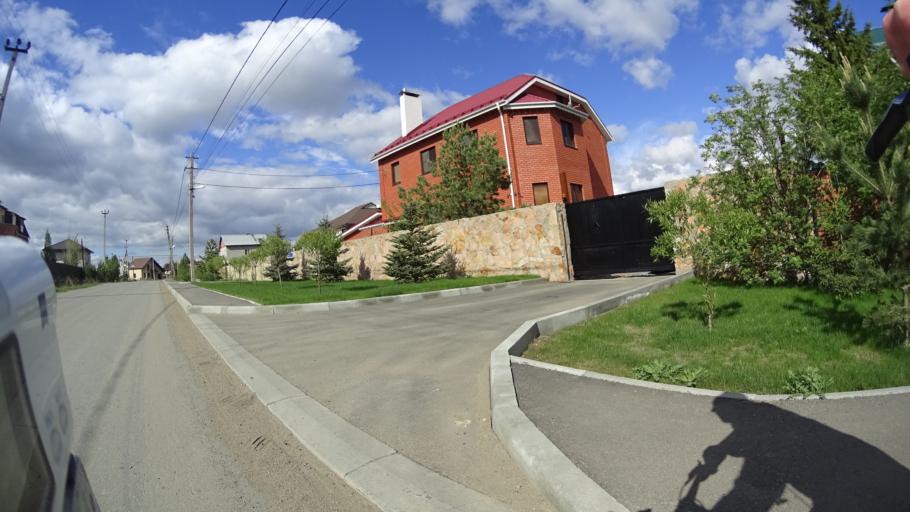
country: RU
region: Chelyabinsk
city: Sargazy
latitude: 55.1527
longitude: 61.2400
